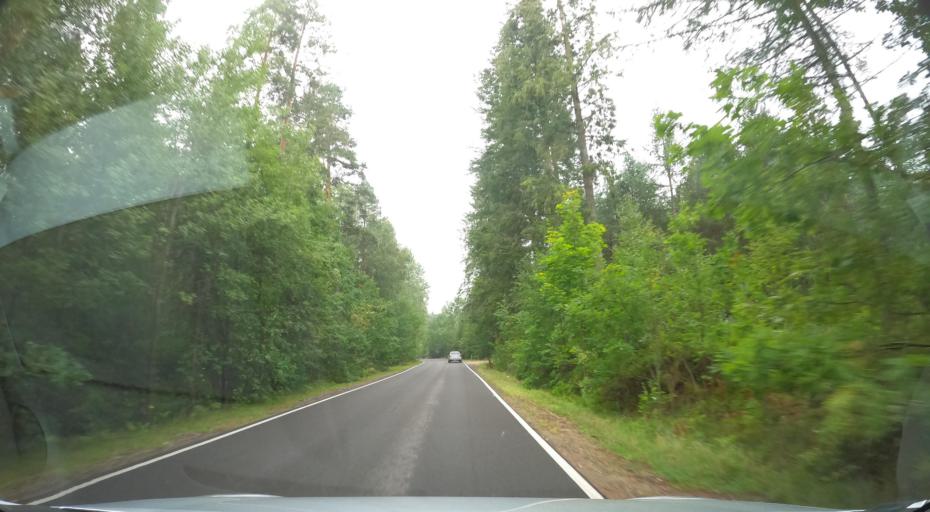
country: PL
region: Pomeranian Voivodeship
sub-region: Powiat wejherowski
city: Linia
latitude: 54.4908
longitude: 17.8421
